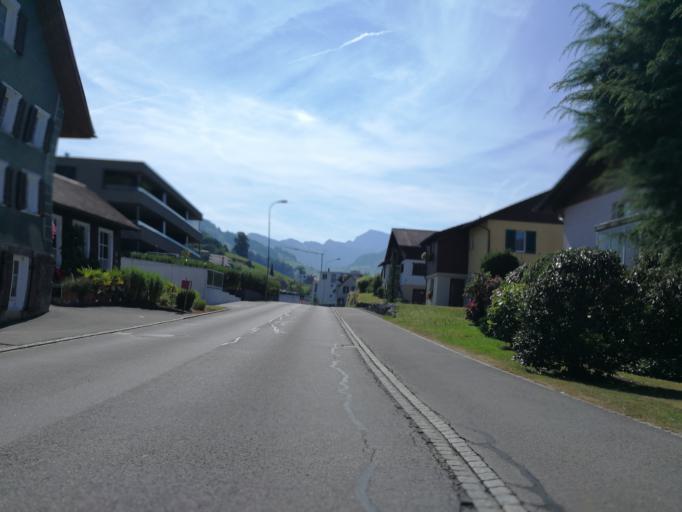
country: CH
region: Saint Gallen
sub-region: Wahlkreis See-Gaster
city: Gommiswald
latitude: 47.2358
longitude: 9.0195
